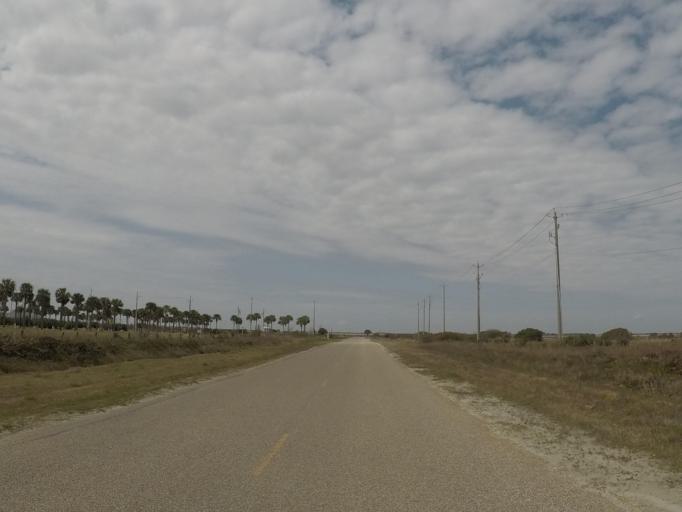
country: US
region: Texas
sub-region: Galveston County
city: Galveston
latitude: 29.3256
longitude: -94.7419
